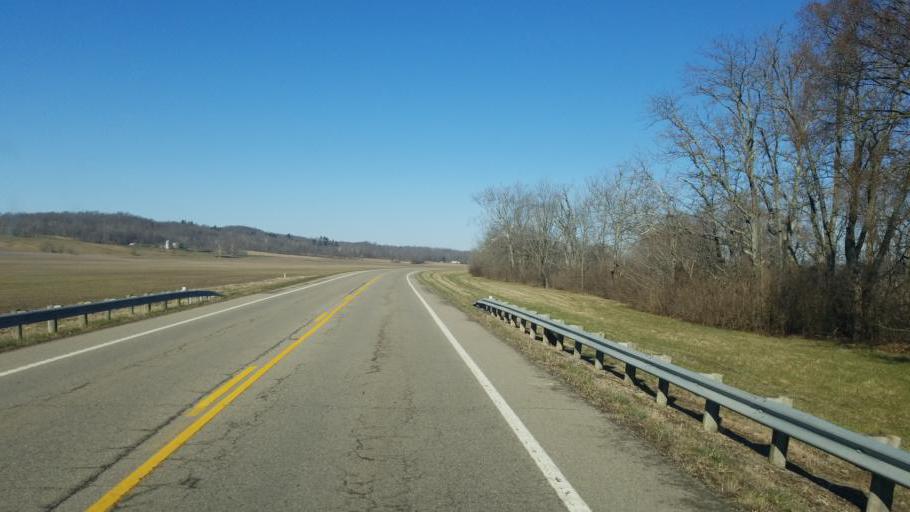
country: US
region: Ohio
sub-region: Highland County
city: Greenfield
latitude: 39.2210
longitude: -83.2948
